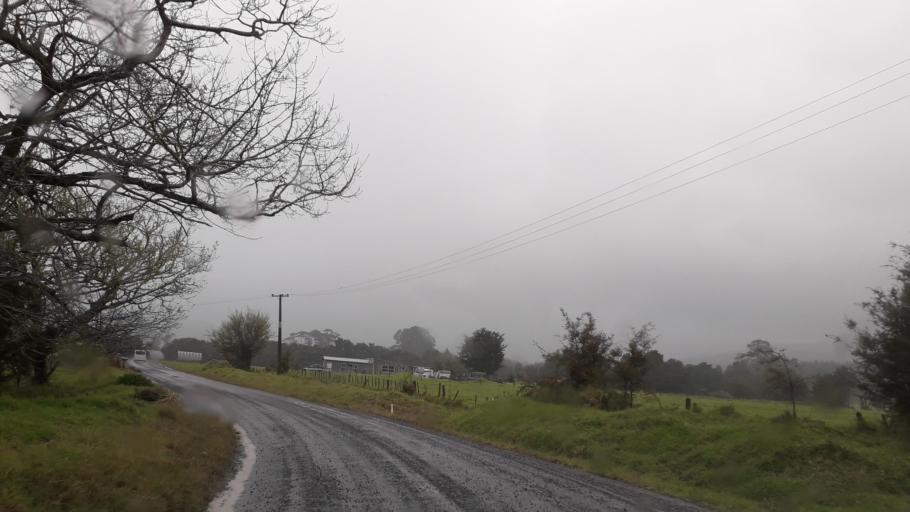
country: NZ
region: Northland
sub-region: Far North District
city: Waimate North
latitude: -35.5008
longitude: 173.6986
